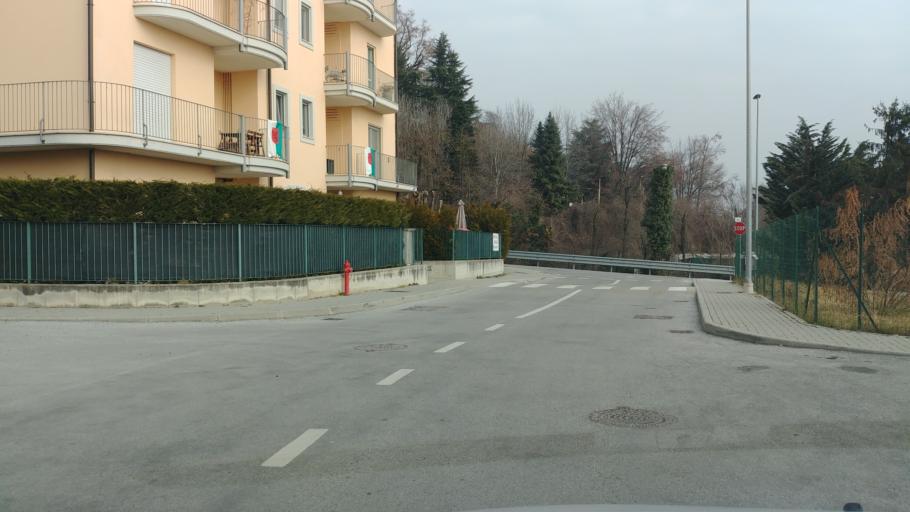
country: IT
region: Piedmont
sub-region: Provincia di Cuneo
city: Fossano
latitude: 44.5455
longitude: 7.7261
